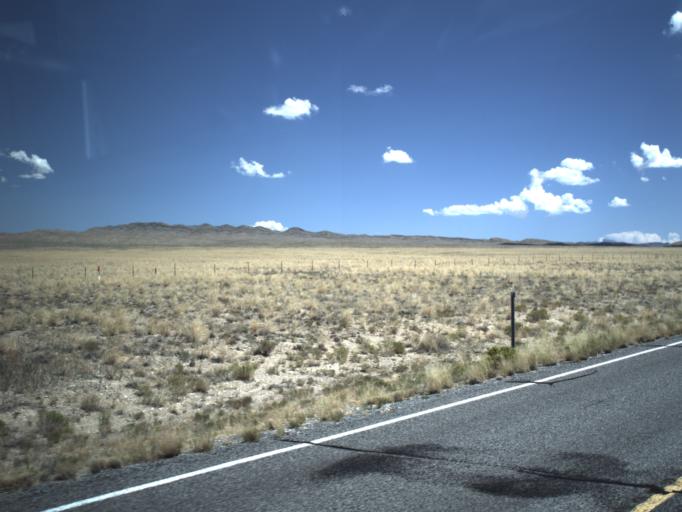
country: US
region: Nevada
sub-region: White Pine County
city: McGill
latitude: 39.0436
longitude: -113.8722
